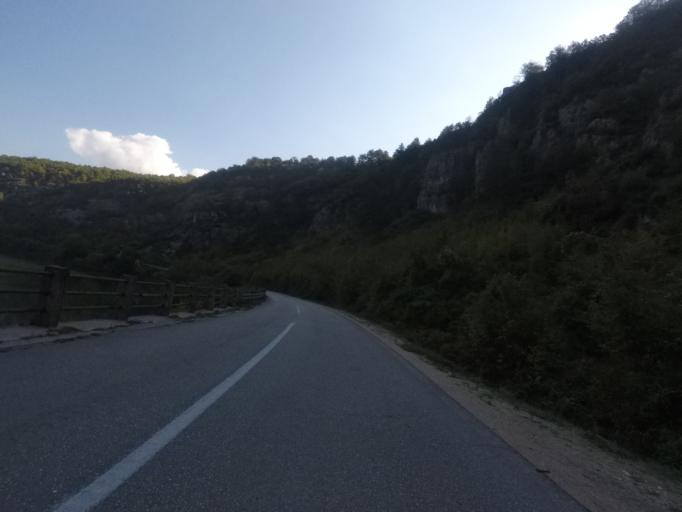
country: BA
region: Republika Srpska
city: Trebinje
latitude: 42.7035
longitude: 18.4786
